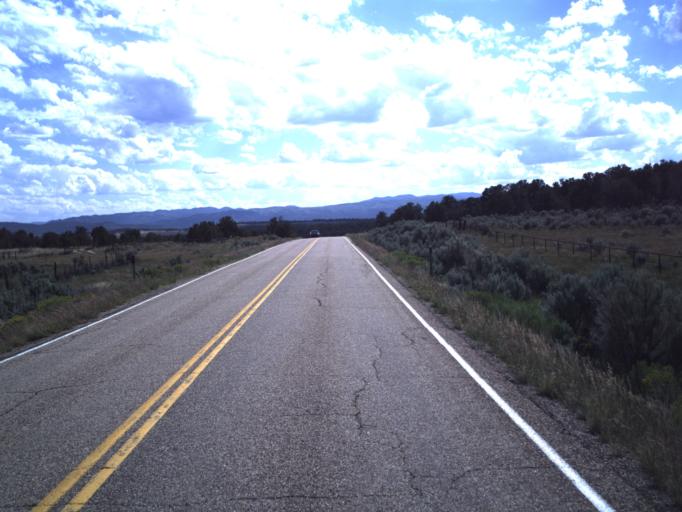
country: US
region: Utah
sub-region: Duchesne County
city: Duchesne
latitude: 40.2855
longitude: -110.6989
